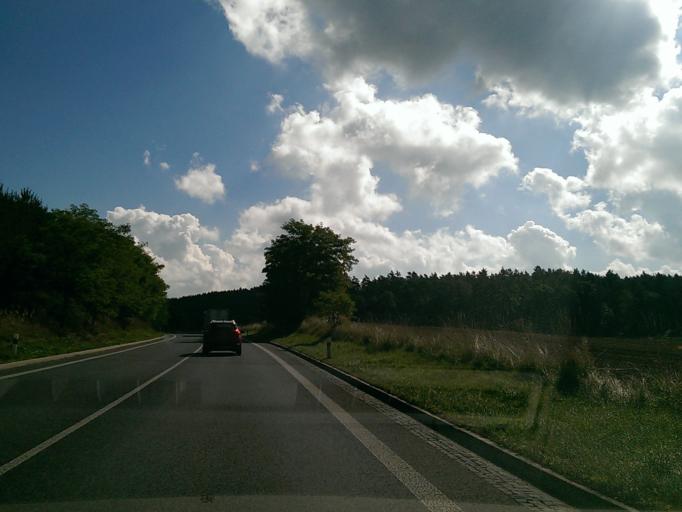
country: CZ
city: Doksy
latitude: 50.6005
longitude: 14.5951
